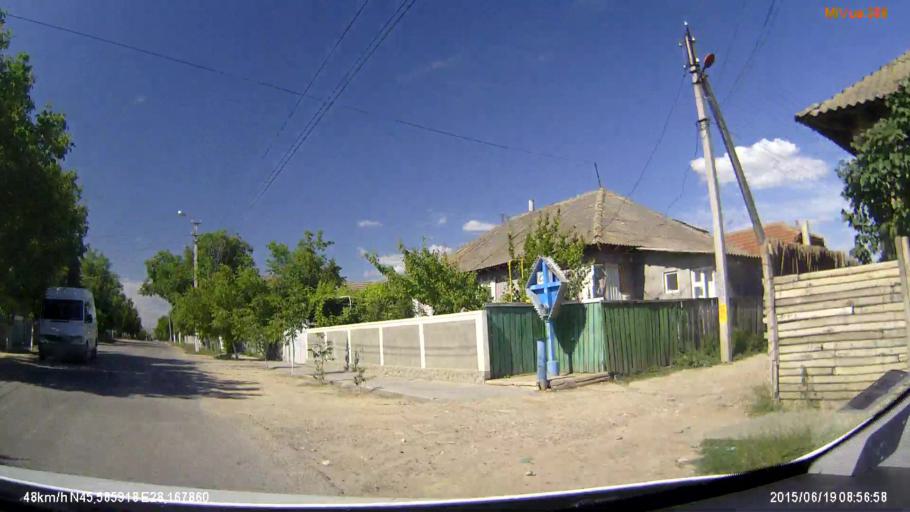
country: MD
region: Cahul
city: Giurgiulesti
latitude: 45.5858
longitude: 28.1679
